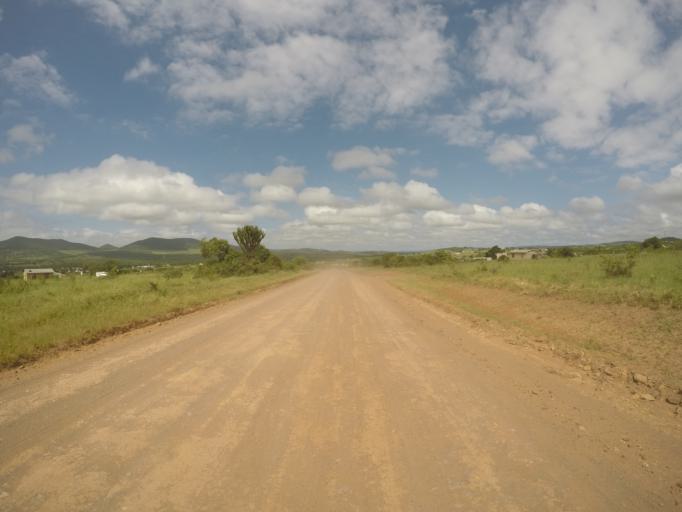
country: ZA
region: KwaZulu-Natal
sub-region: uThungulu District Municipality
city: Empangeni
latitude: -28.6083
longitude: 31.8472
